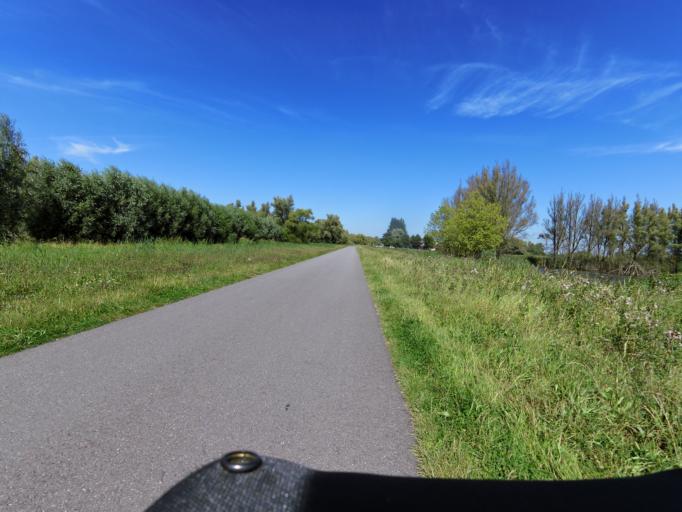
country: NL
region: South Holland
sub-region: Gemeente Sliedrecht
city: Sliedrecht
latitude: 51.7742
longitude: 4.7579
